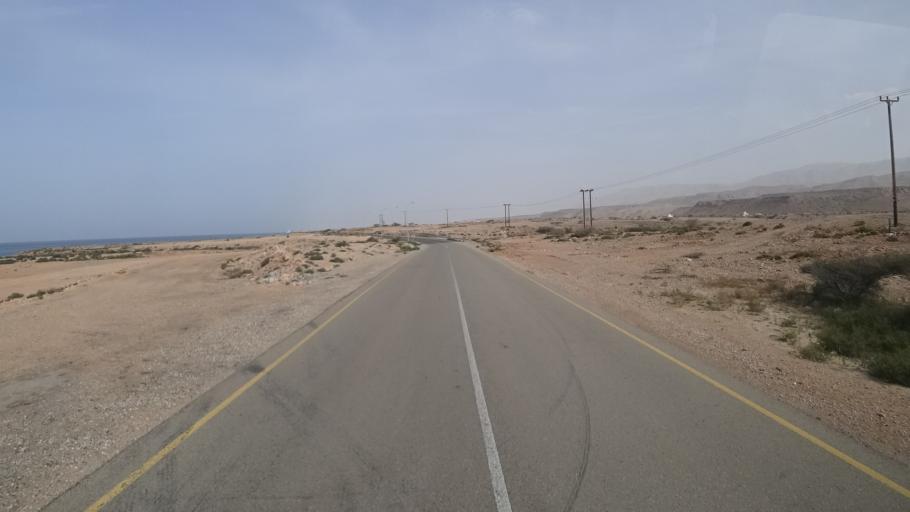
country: OM
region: Ash Sharqiyah
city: Al Qabil
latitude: 23.0067
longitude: 59.1126
